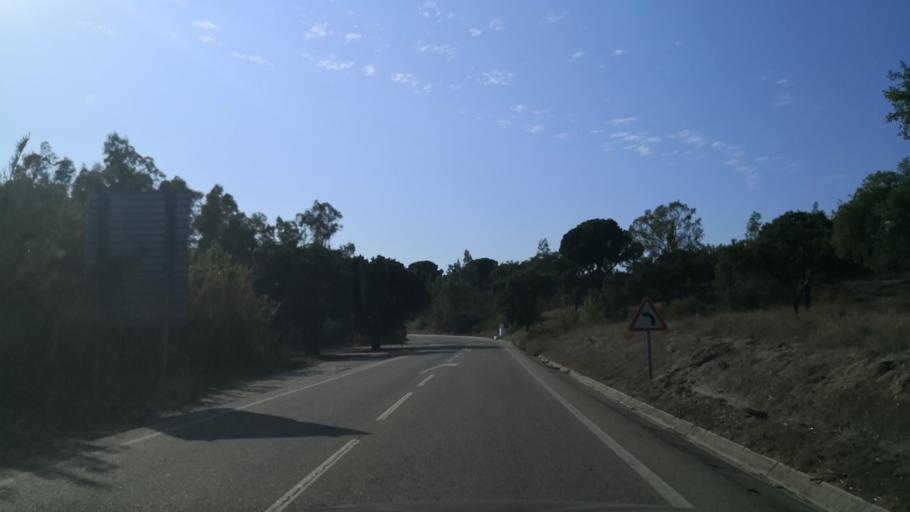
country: PT
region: Santarem
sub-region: Almeirim
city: Fazendas de Almeirim
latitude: 39.1150
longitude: -8.5799
